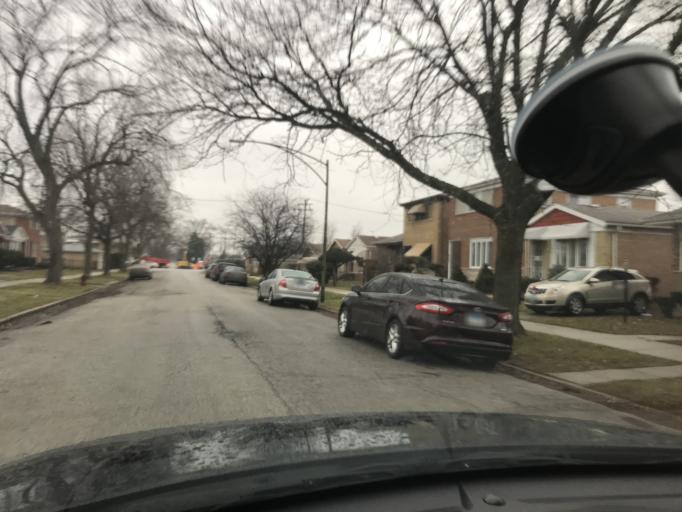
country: US
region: Illinois
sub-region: Cook County
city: Calumet Park
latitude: 41.7204
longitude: -87.6383
